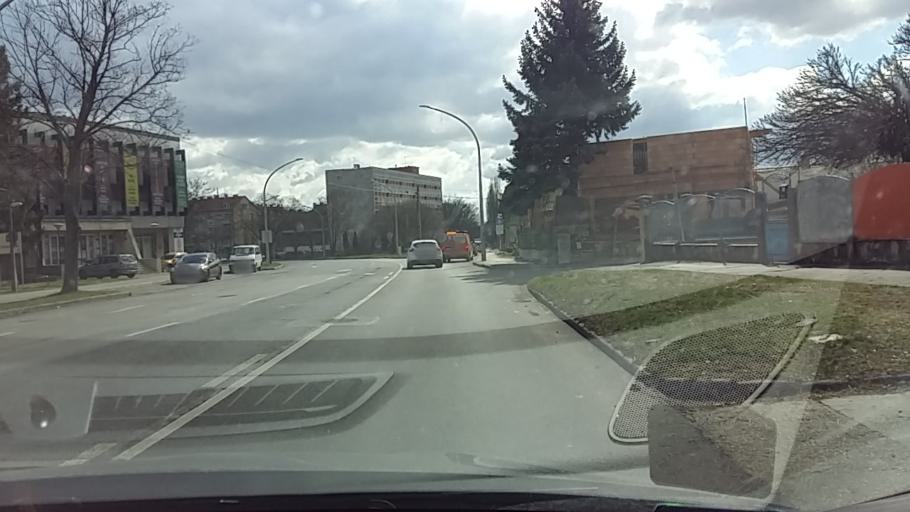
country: HU
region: Baranya
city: Pellerd
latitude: 46.0646
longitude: 18.1898
